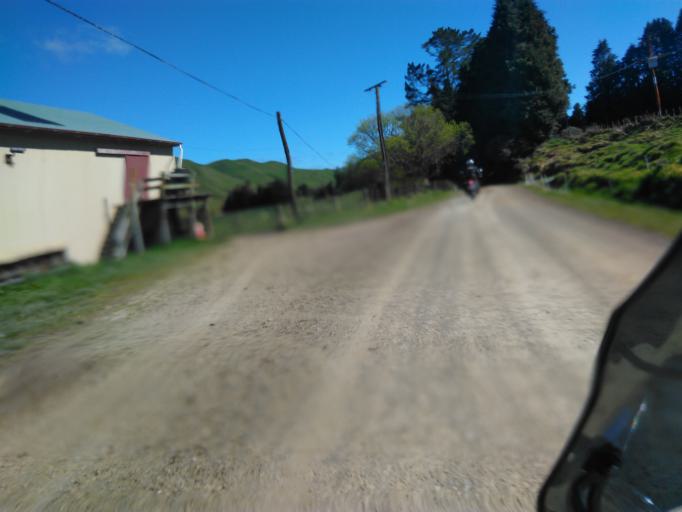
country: NZ
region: Bay of Plenty
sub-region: Opotiki District
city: Opotiki
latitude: -38.2935
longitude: 177.5492
